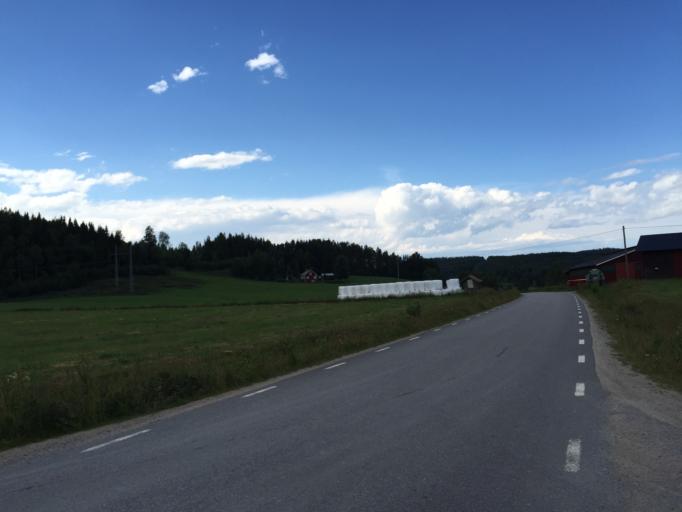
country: SE
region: Gaevleborg
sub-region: Ljusdals Kommun
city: Jaervsoe
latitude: 61.7375
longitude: 16.2791
